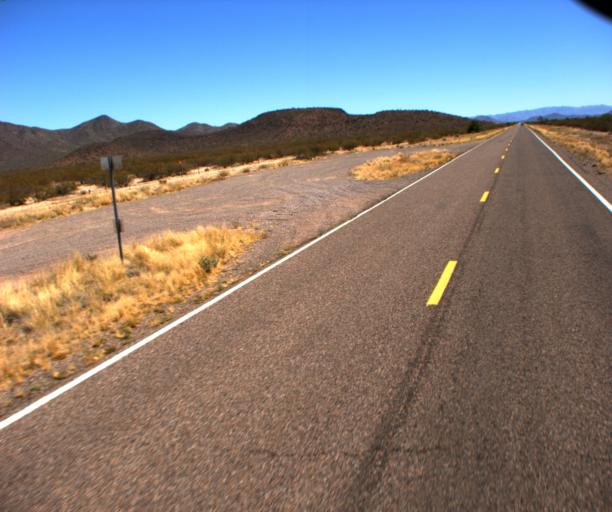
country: US
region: Arizona
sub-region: Yavapai County
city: Congress
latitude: 33.9998
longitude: -113.1220
